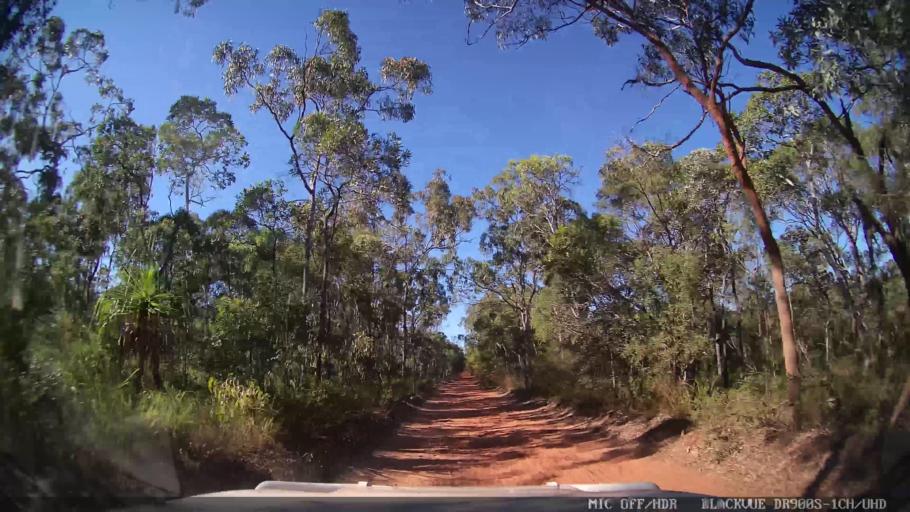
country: AU
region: Queensland
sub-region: Torres
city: Thursday Island
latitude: -11.4086
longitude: 142.4082
